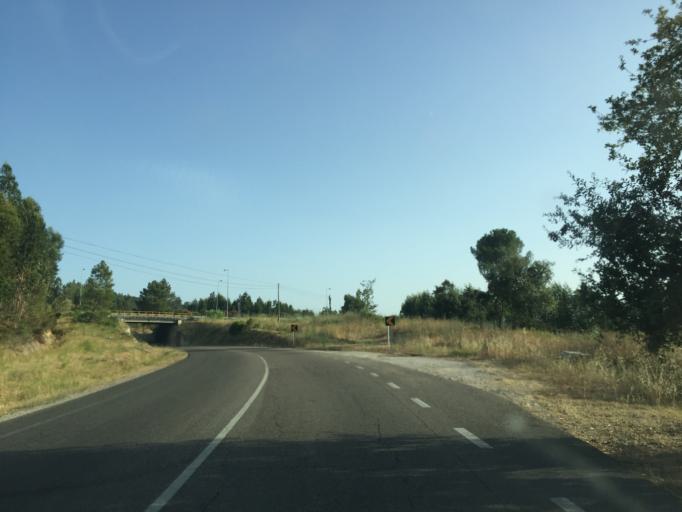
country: PT
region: Santarem
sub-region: Entroncamento
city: Entroncamento
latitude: 39.4903
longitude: -8.4438
